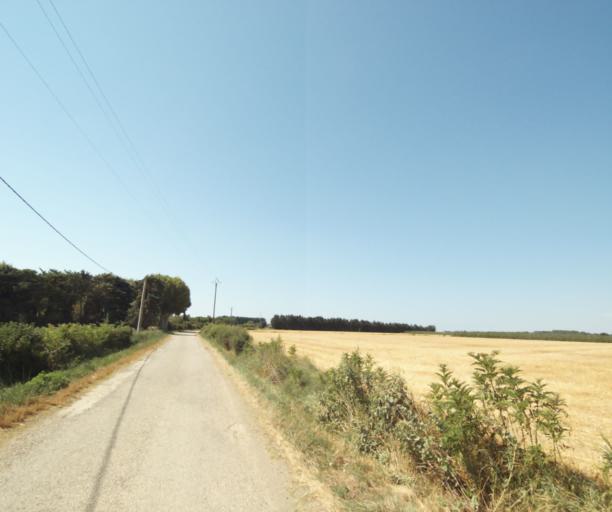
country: FR
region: Languedoc-Roussillon
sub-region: Departement de l'Herault
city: Marsillargues
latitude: 43.6477
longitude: 4.1621
